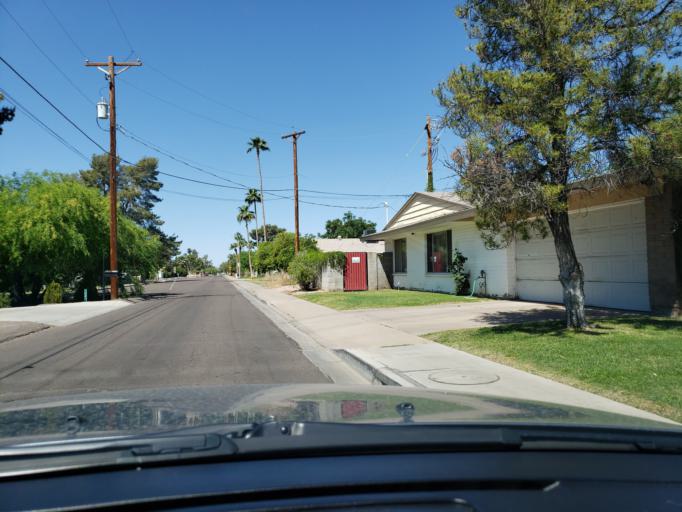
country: US
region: Arizona
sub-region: Maricopa County
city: Glendale
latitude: 33.5604
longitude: -112.0930
